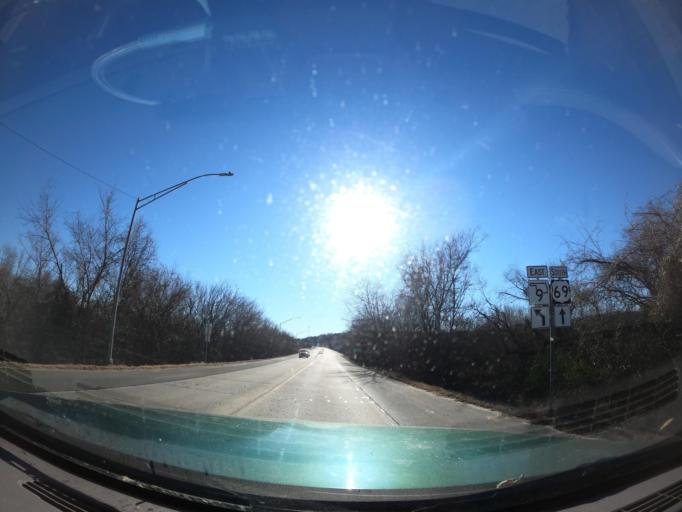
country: US
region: Oklahoma
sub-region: McIntosh County
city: Eufaula
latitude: 35.2762
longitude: -95.5846
